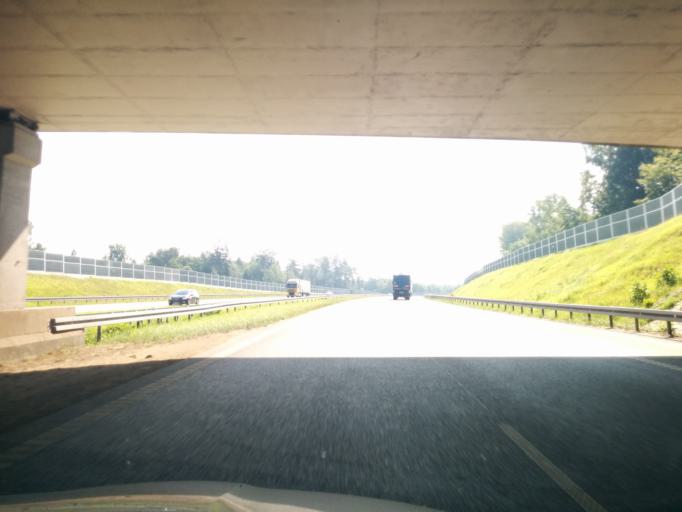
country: PL
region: Silesian Voivodeship
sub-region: Powiat tarnogorski
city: Tarnowskie Gory
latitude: 50.3875
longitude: 18.8401
